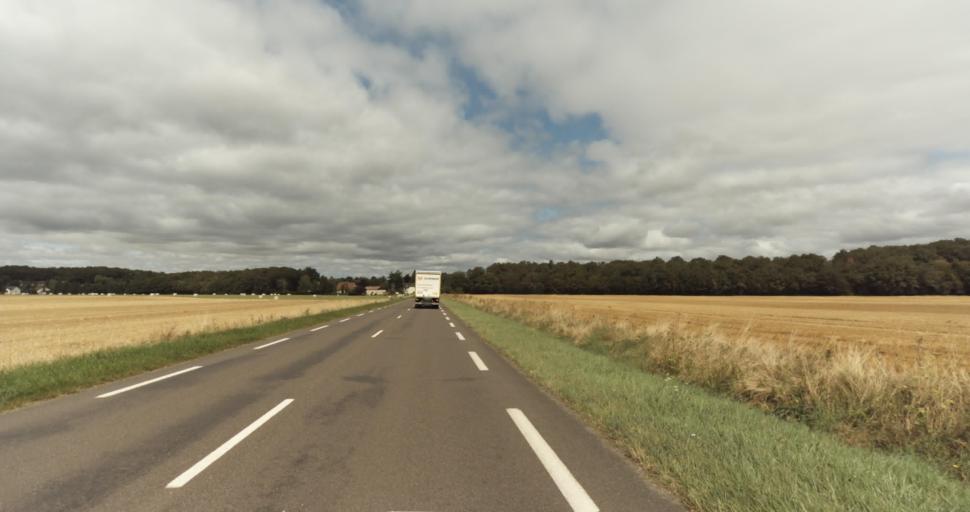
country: FR
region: Haute-Normandie
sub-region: Departement de l'Eure
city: Evreux
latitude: 48.9672
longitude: 1.1601
